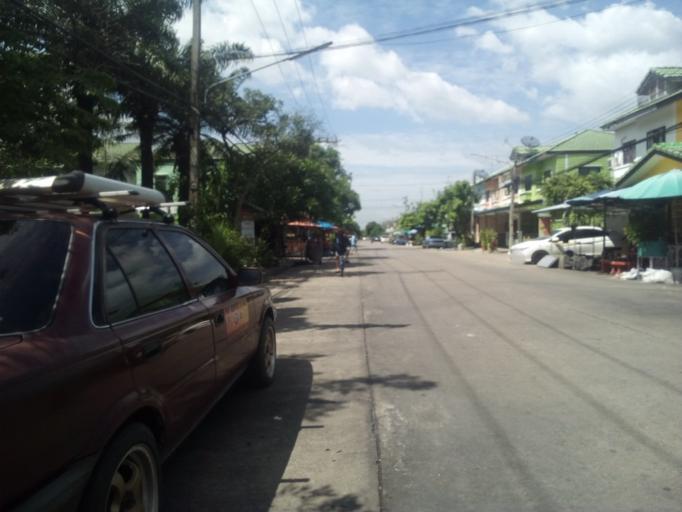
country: TH
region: Pathum Thani
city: Nong Suea
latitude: 14.0526
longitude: 100.8518
